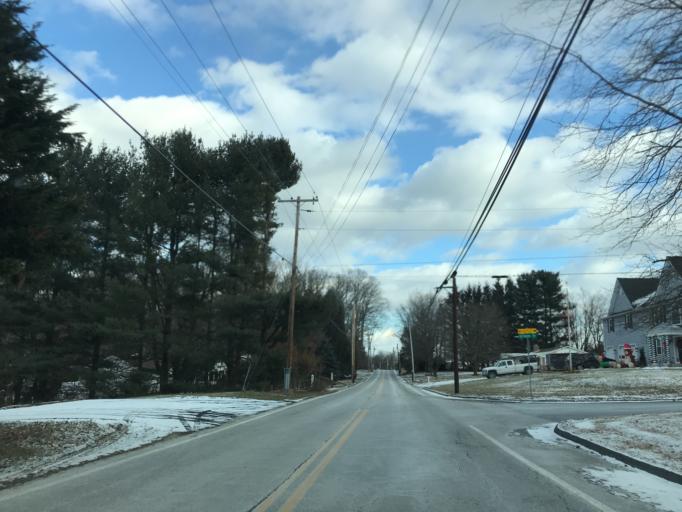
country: US
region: Maryland
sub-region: Harford County
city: Jarrettsville
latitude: 39.6274
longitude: -76.4730
